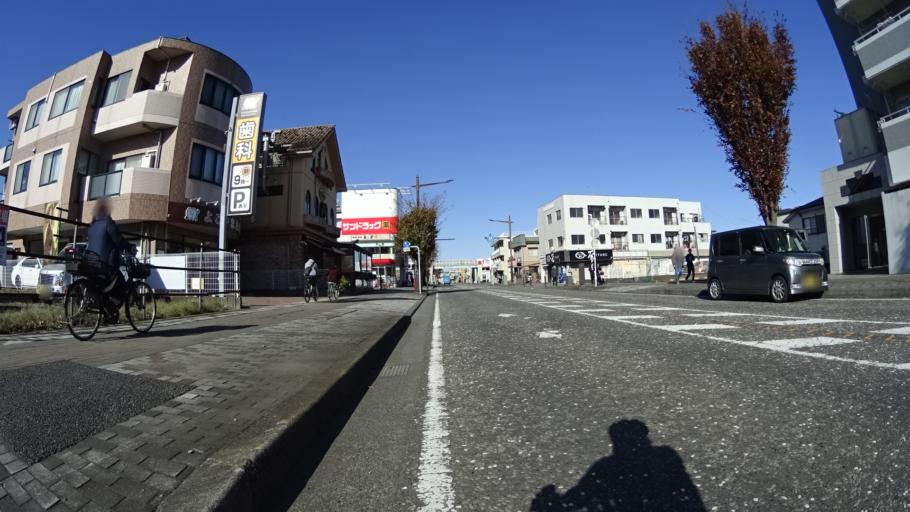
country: JP
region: Kanagawa
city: Zama
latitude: 35.5652
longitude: 139.3608
